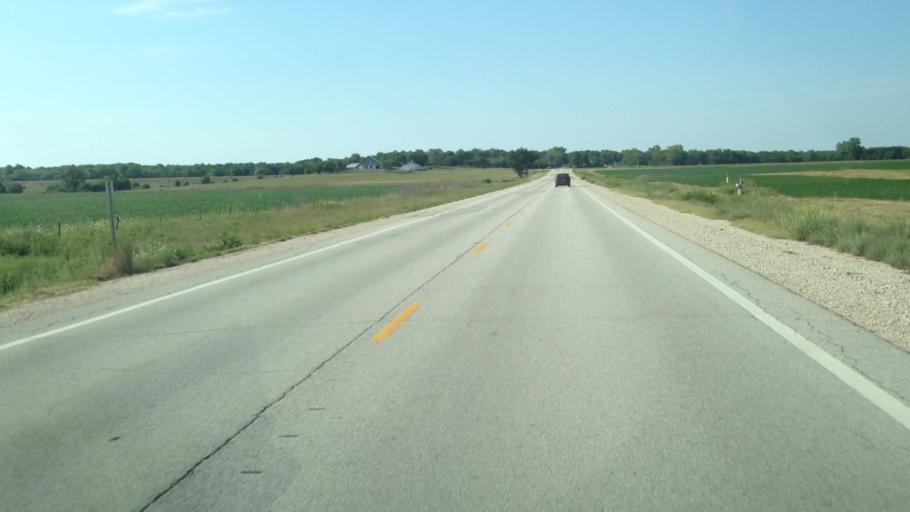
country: US
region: Kansas
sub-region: Anderson County
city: Garnett
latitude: 38.0739
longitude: -95.1694
